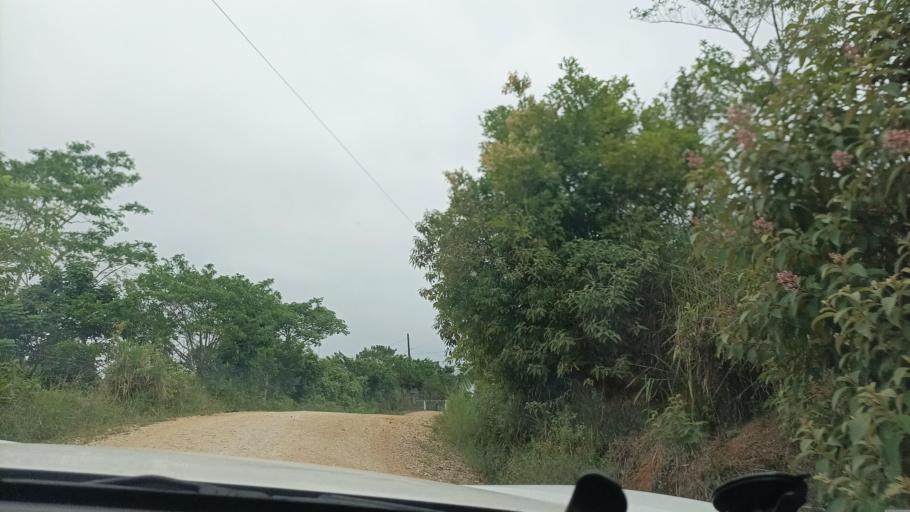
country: MX
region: Veracruz
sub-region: Uxpanapa
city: Poblado Cinco
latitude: 17.4839
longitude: -94.5739
